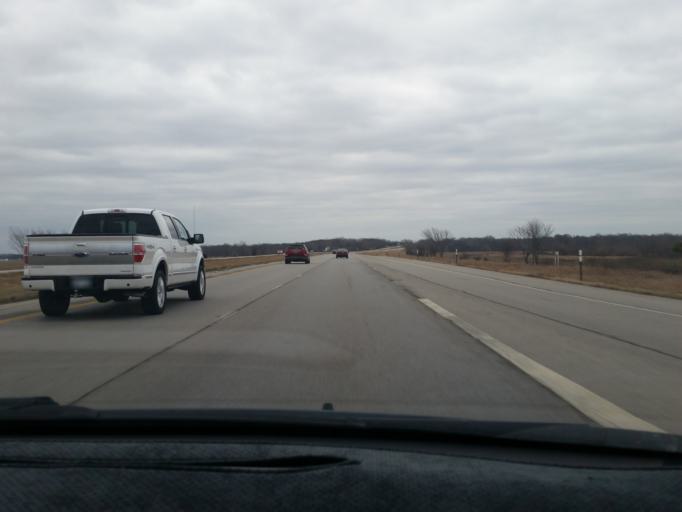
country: US
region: Kansas
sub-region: Douglas County
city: Eudora
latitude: 38.9349
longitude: -95.1459
